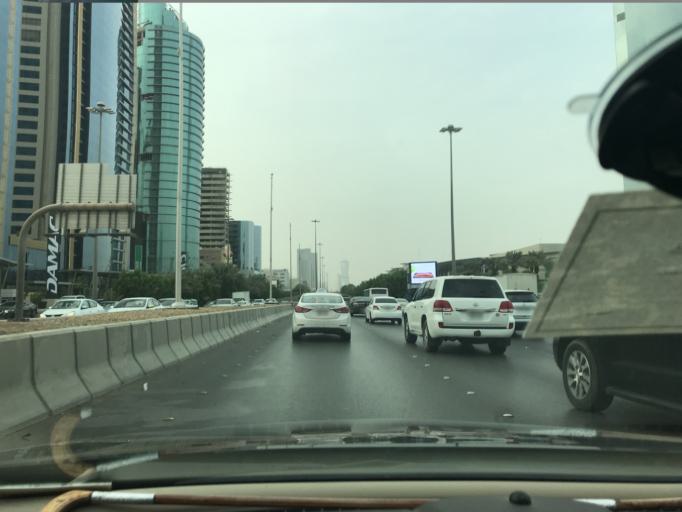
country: SA
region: Ar Riyad
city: Riyadh
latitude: 24.7084
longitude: 46.6739
